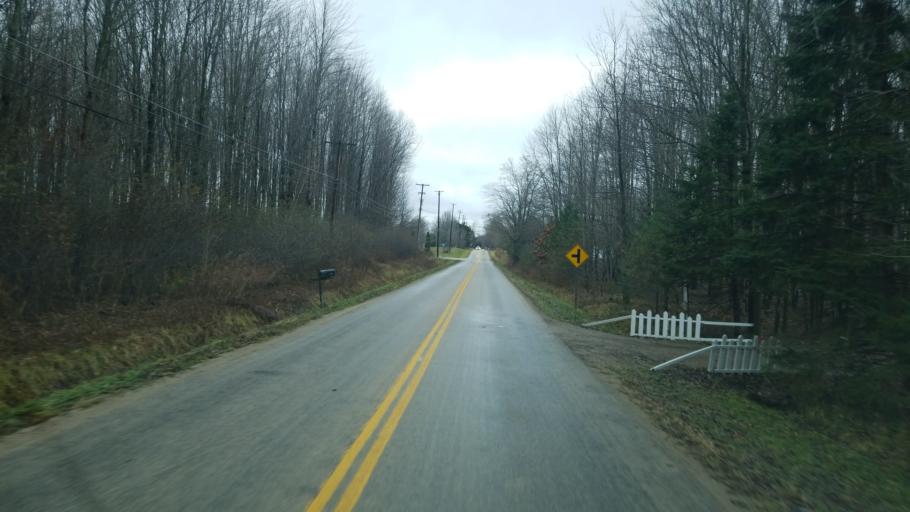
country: US
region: Ohio
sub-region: Ashtabula County
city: North Kingsville
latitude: 41.8219
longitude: -80.6263
